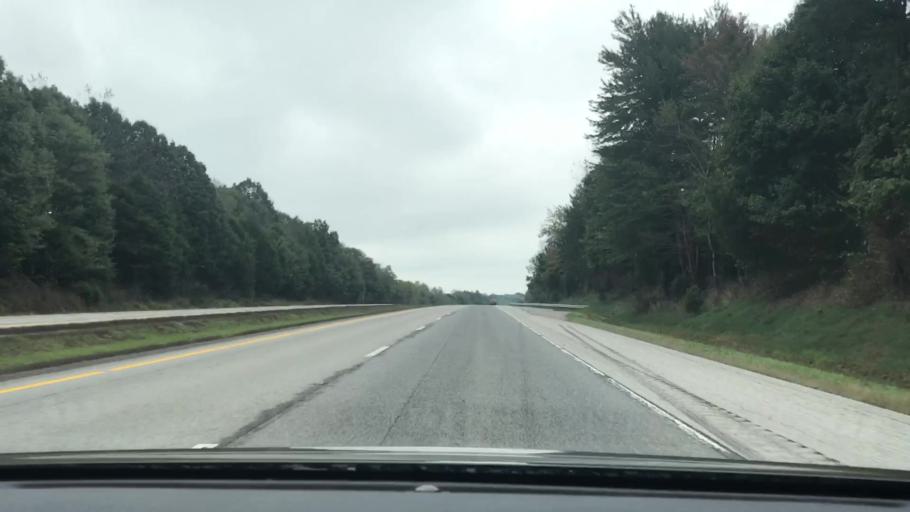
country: US
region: Kentucky
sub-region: Metcalfe County
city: Edmonton
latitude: 36.9972
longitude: -85.7397
